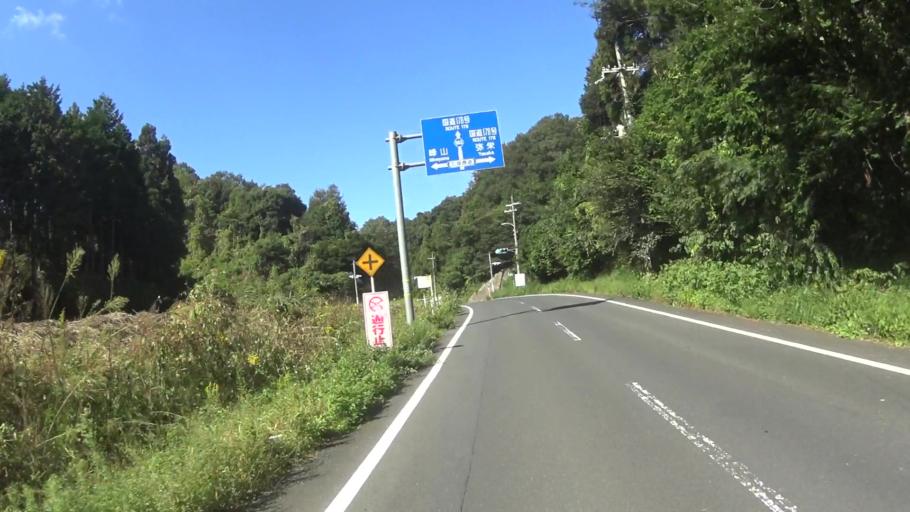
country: JP
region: Kyoto
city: Miyazu
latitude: 35.6599
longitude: 135.0637
